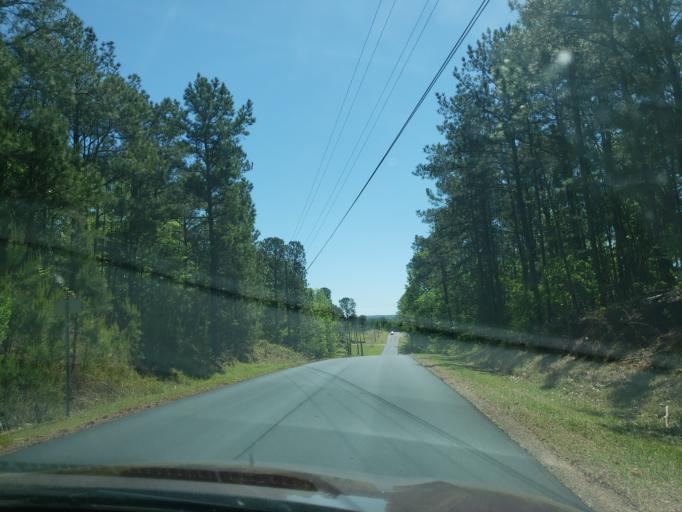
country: US
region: Alabama
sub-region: Tallapoosa County
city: Dadeville
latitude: 32.7025
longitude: -85.8713
